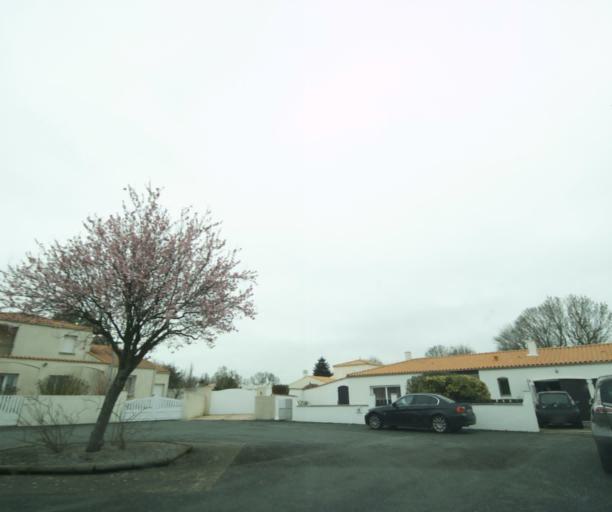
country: FR
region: Poitou-Charentes
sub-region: Departement de la Charente-Maritime
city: Lagord
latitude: 46.1867
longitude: -1.1419
